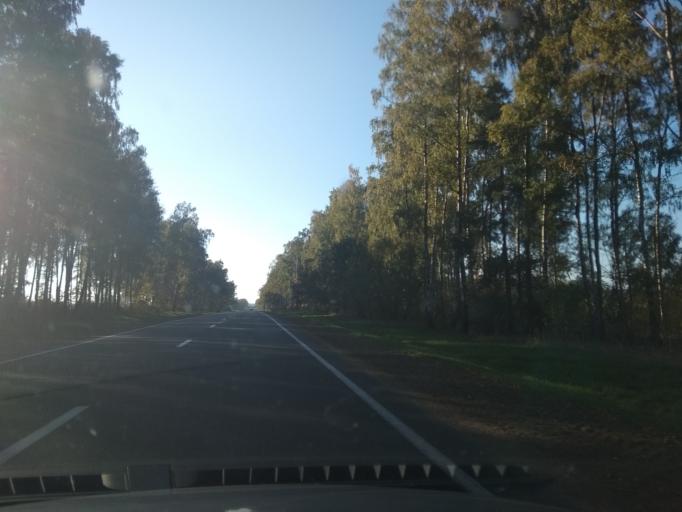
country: BY
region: Grodnenskaya
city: Vyalikaya Byerastavitsa
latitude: 53.1176
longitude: 24.0116
